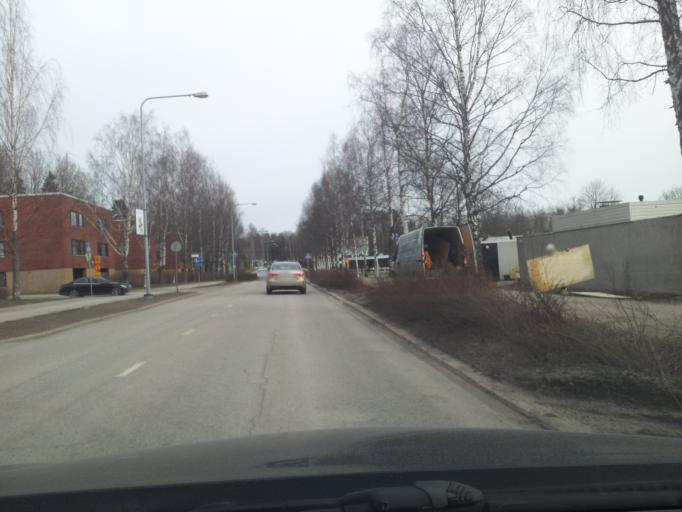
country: FI
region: Uusimaa
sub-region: Helsinki
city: Otaniemi
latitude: 60.1843
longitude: 24.7955
